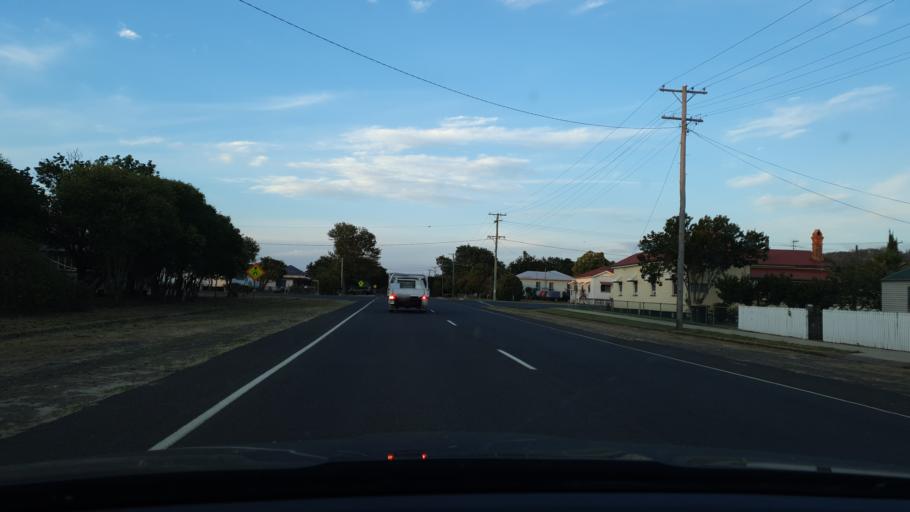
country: AU
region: Queensland
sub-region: Southern Downs
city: Warwick
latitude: -28.0339
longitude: 151.9806
